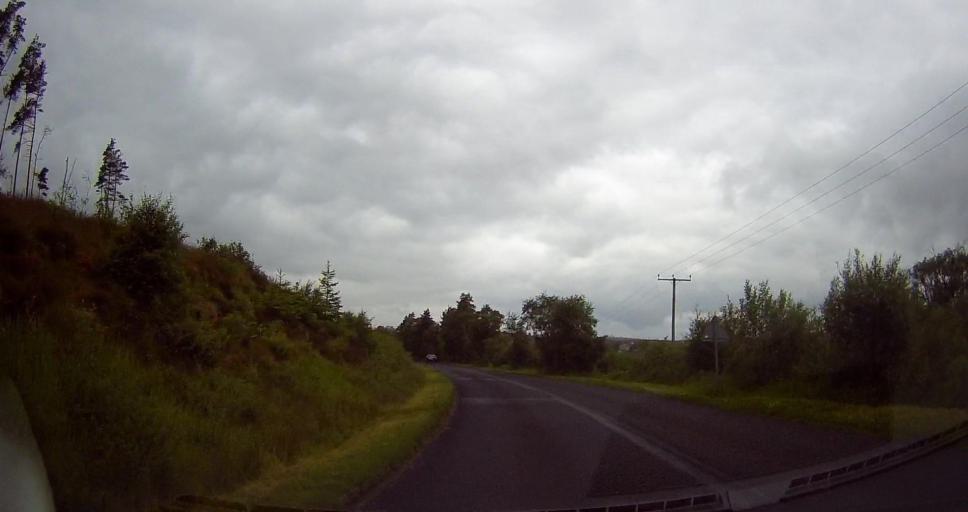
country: GB
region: Scotland
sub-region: Highland
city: Alness
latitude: 58.0231
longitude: -4.3792
